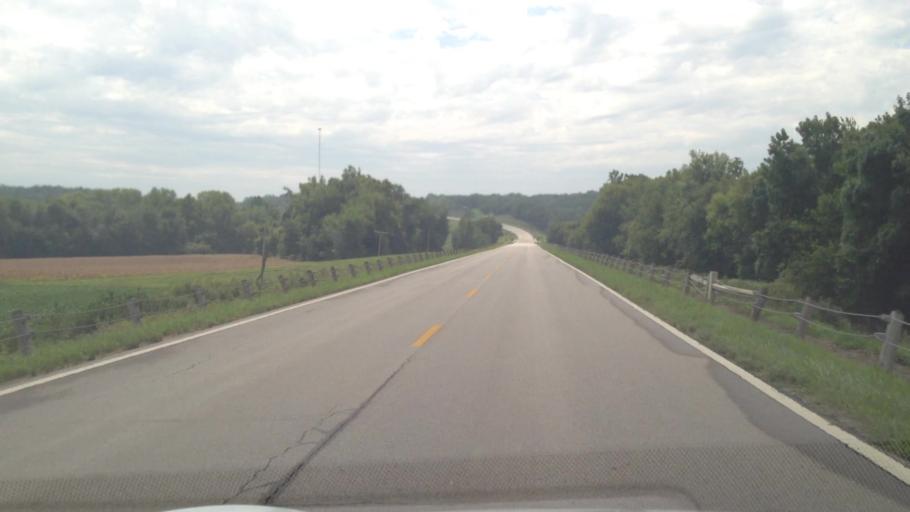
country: US
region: Kansas
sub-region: Bourbon County
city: Fort Scott
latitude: 37.8389
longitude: -94.9813
